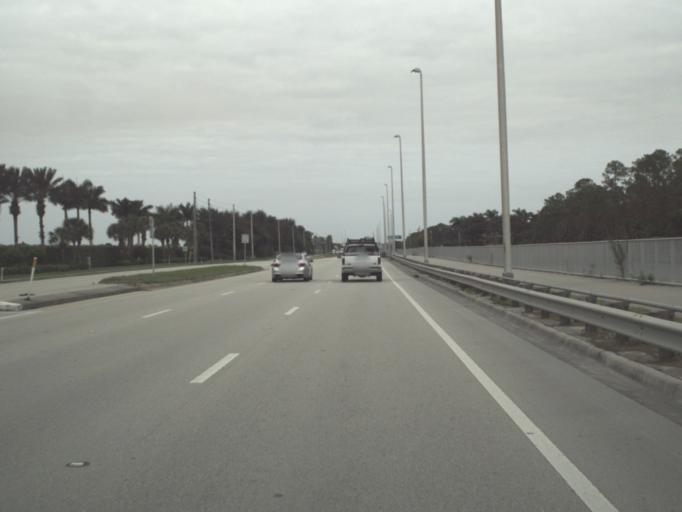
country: US
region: Florida
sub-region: Collier County
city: Golden Gate
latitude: 26.1415
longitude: -81.6867
